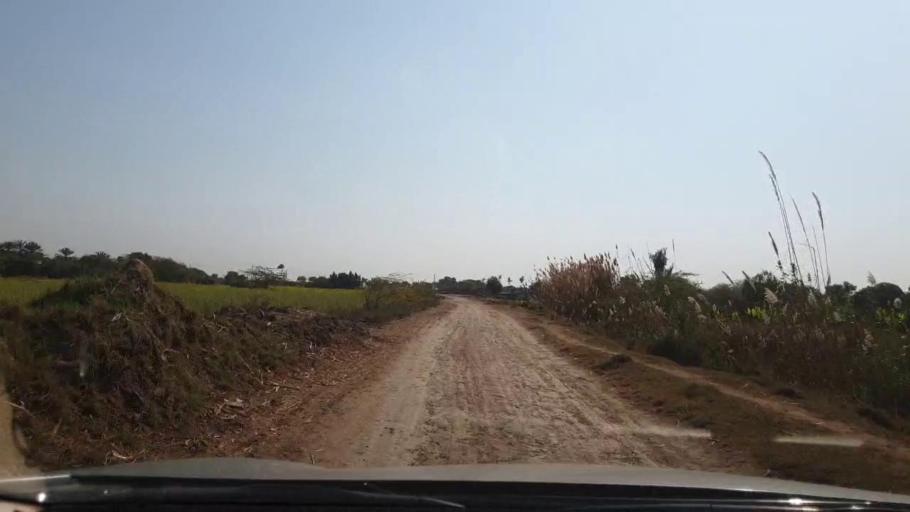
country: PK
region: Sindh
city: Mirpur Khas
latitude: 25.5927
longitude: 68.8673
